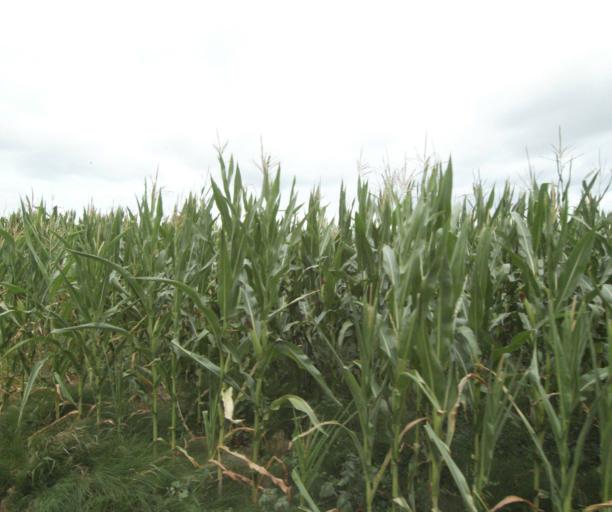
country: FR
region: Nord-Pas-de-Calais
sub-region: Departement du Nord
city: Linselles
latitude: 50.7373
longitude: 3.0998
